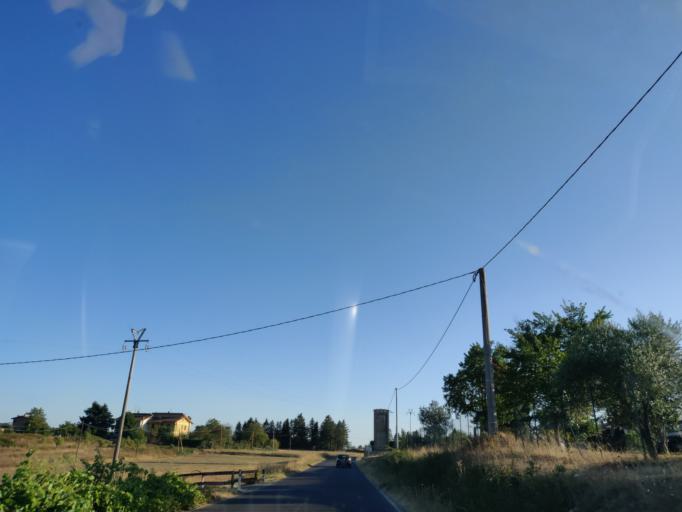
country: IT
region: Latium
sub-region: Provincia di Viterbo
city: Acquapendente
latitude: 42.7335
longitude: 11.8767
